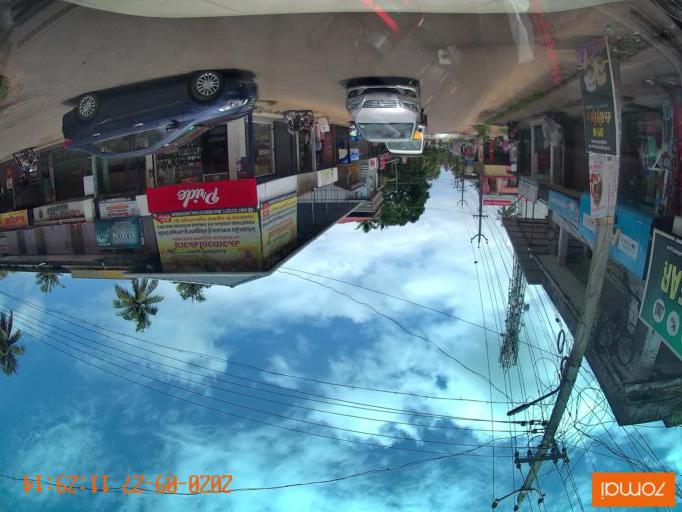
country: IN
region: Kerala
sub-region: Thrissur District
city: Thanniyam
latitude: 10.4161
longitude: 76.1352
